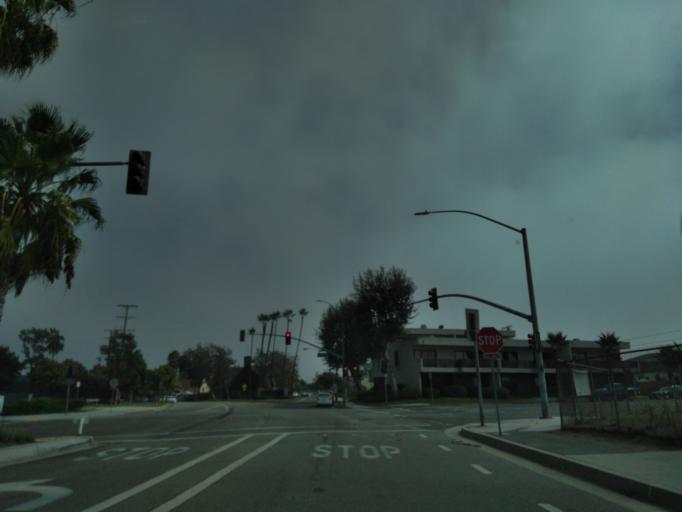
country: US
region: California
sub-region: Orange County
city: Seal Beach
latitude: 33.7457
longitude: -118.1116
